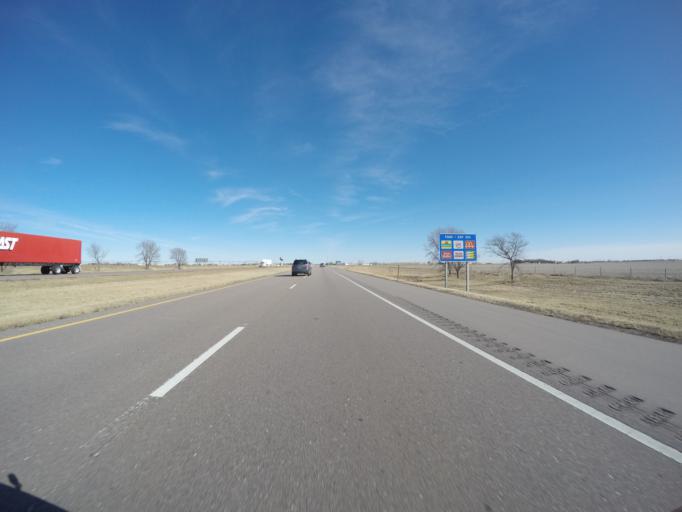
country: US
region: Nebraska
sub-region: York County
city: York
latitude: 40.8211
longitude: -97.6156
